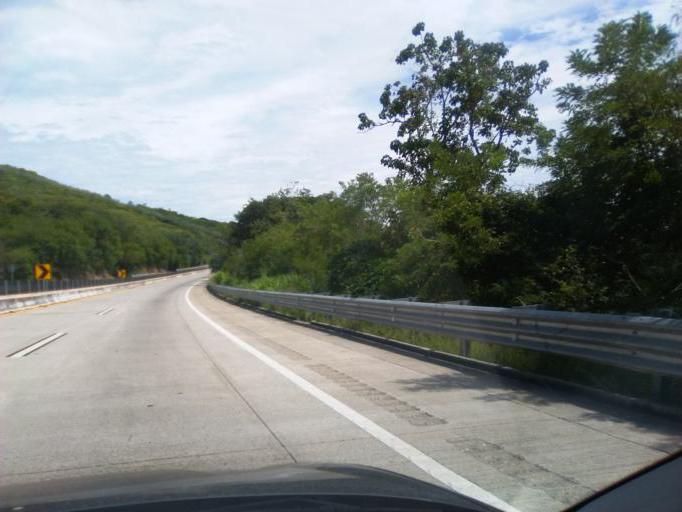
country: MX
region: Guerrero
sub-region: Acapulco de Juarez
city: Pueblo Madero (El Playon)
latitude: 17.0748
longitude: -99.6169
